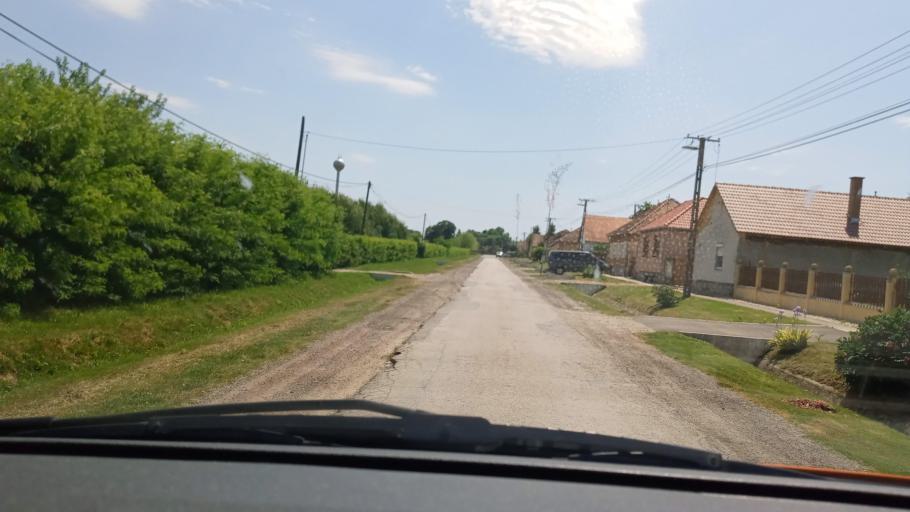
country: HU
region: Baranya
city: Harkany
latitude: 45.8320
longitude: 18.1370
